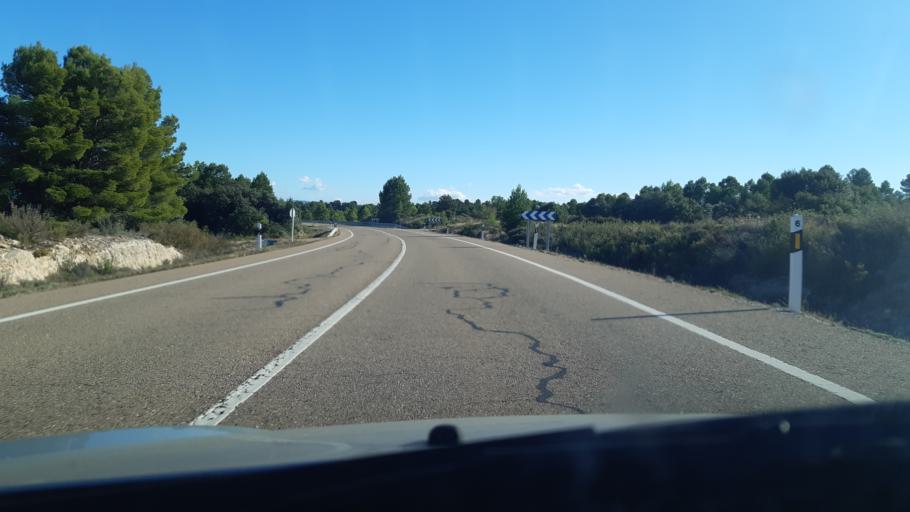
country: ES
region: Aragon
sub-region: Provincia de Teruel
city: Valjunquera
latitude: 40.9542
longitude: -0.0148
